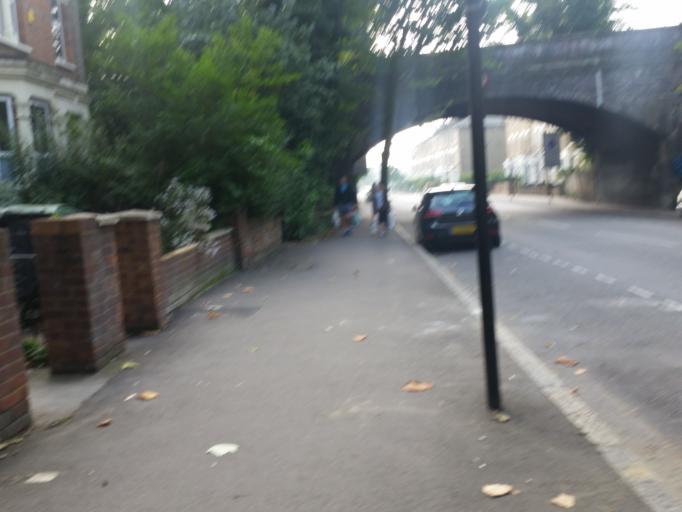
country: GB
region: England
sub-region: Greater London
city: Harringay
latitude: 51.5713
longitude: -0.1073
